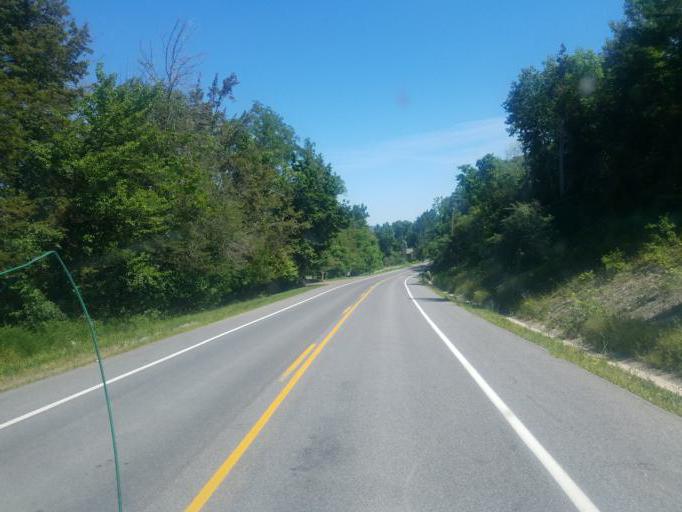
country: US
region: New York
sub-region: Ontario County
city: Canandaigua
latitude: 42.7718
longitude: -77.2964
